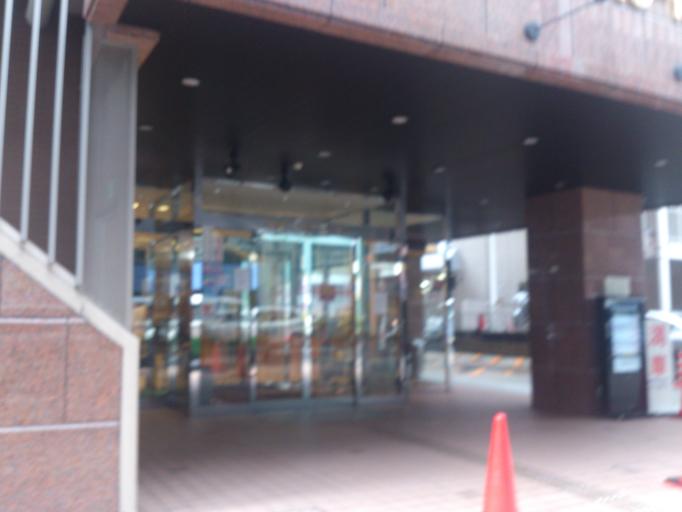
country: JP
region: Hyogo
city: Kobe
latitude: 34.6953
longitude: 135.1980
